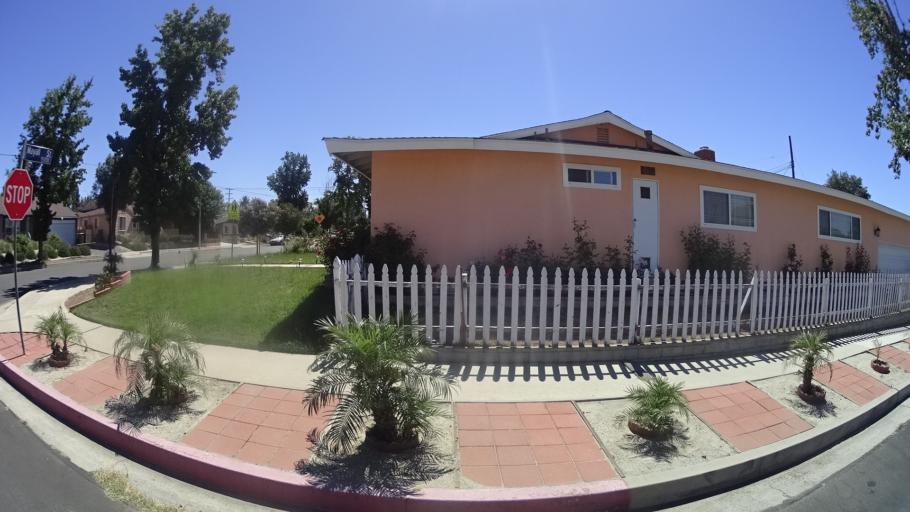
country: US
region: California
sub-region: Los Angeles County
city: San Fernando
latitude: 34.2533
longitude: -118.4599
